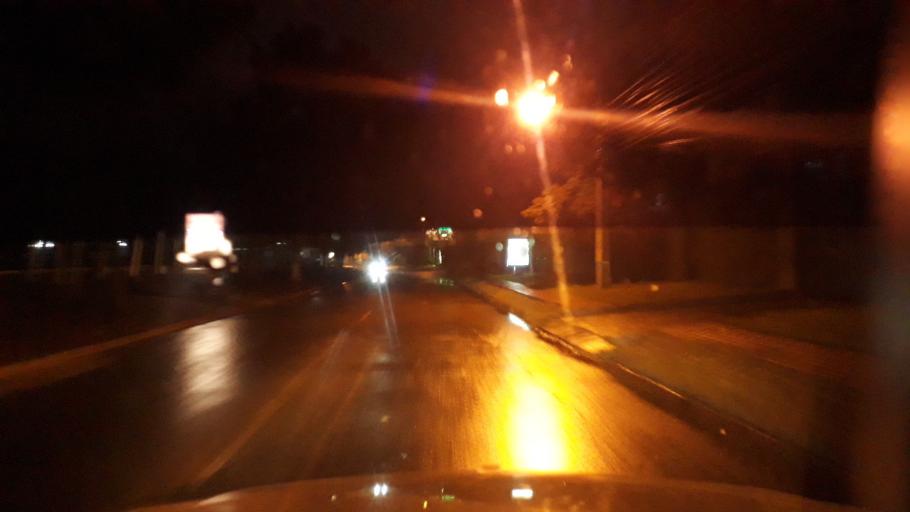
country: HN
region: Cortes
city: El Zapotal del Norte
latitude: 15.5244
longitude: -88.0358
